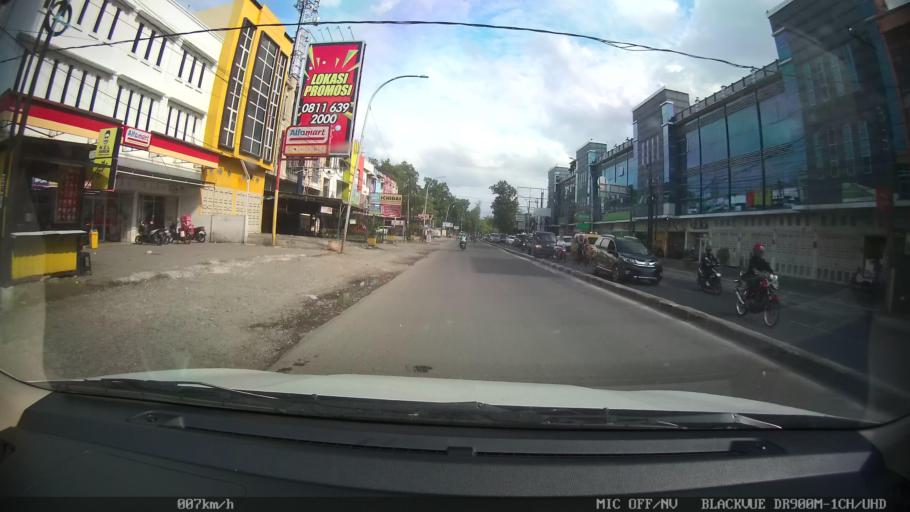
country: ID
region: North Sumatra
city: Medan
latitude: 3.6223
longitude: 98.6701
